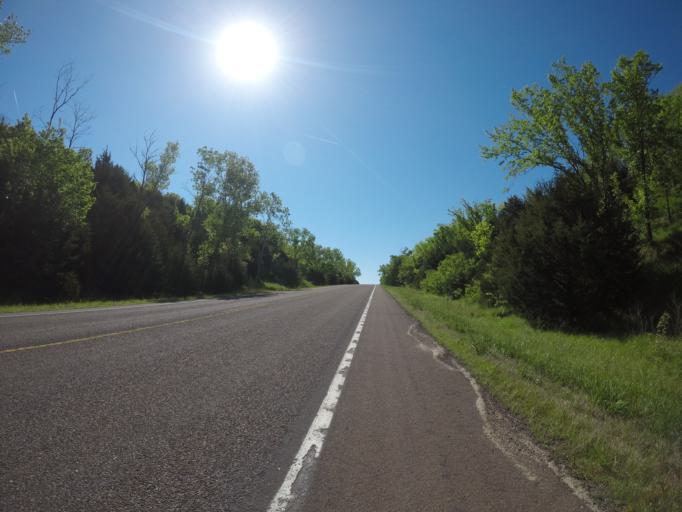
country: US
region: Kansas
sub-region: Osage County
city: Overbrook
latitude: 38.8946
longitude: -95.4342
